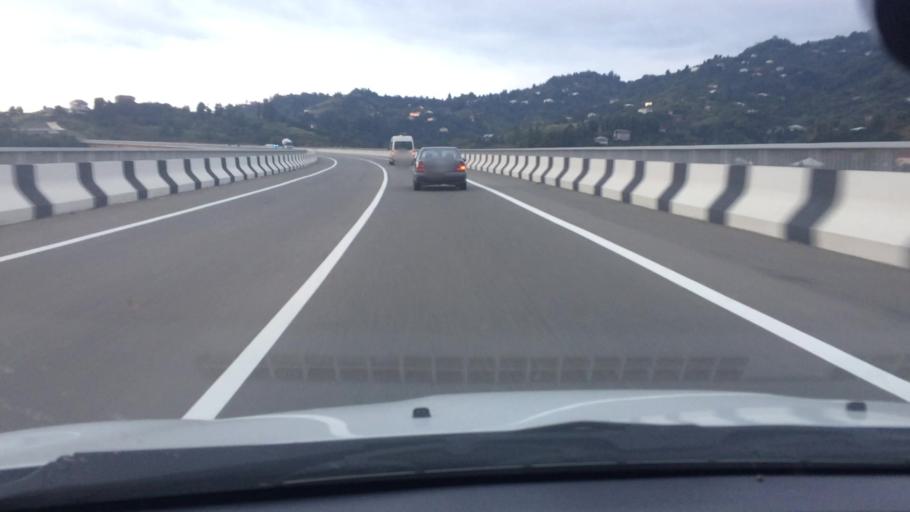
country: GE
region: Ajaria
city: Makhinjauri
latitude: 41.7132
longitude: 41.7522
